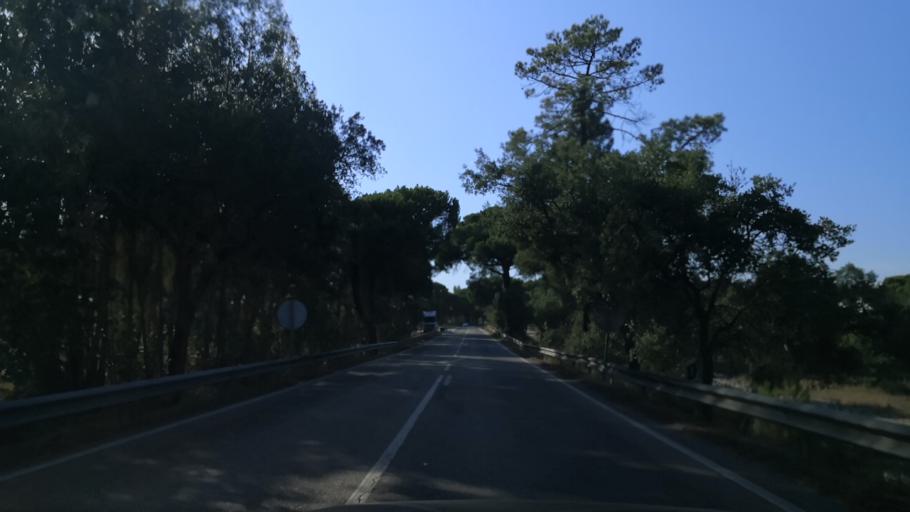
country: PT
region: Santarem
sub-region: Coruche
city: Coruche
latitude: 38.9767
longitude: -8.5410
